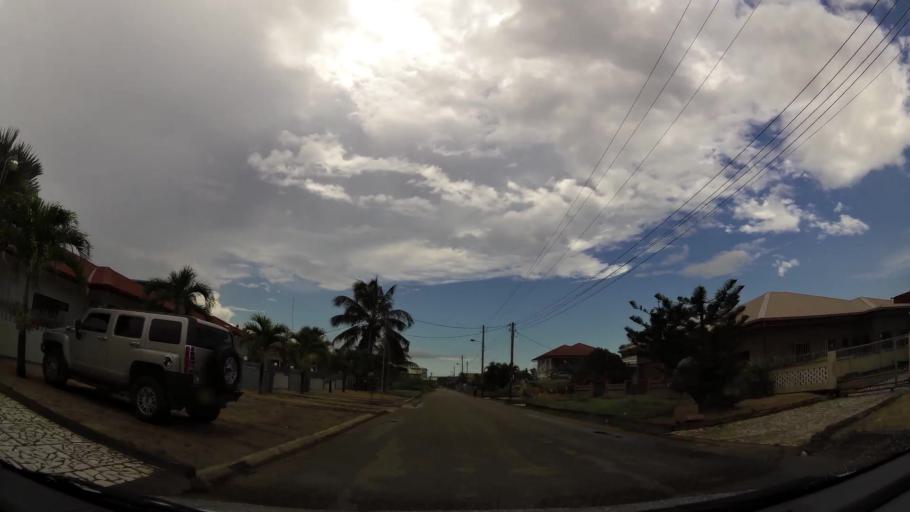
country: SR
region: Paramaribo
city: Paramaribo
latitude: 5.8615
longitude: -55.1229
